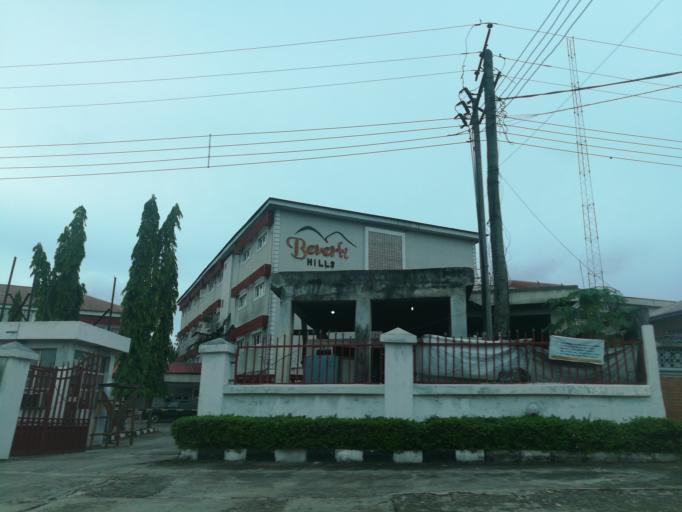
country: NG
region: Rivers
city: Port Harcourt
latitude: 4.8116
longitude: 7.0008
